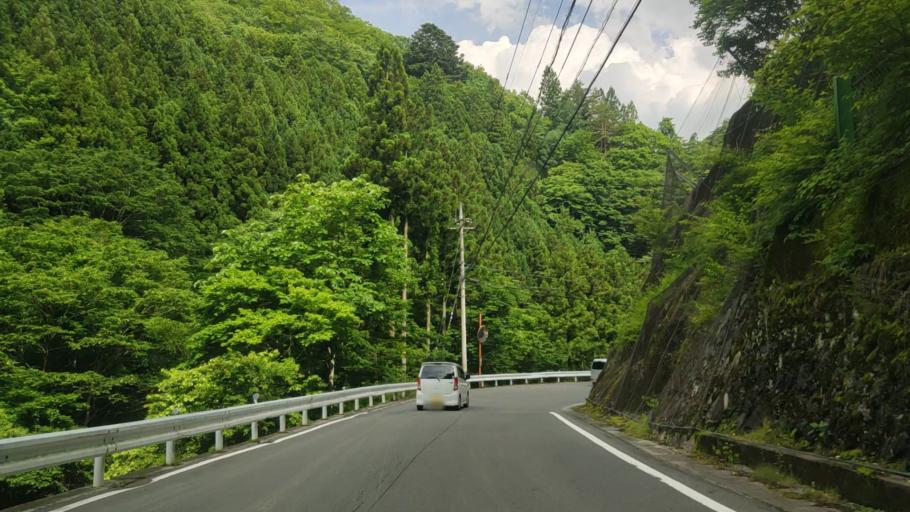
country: JP
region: Gunma
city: Tomioka
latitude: 36.1045
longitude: 138.7173
